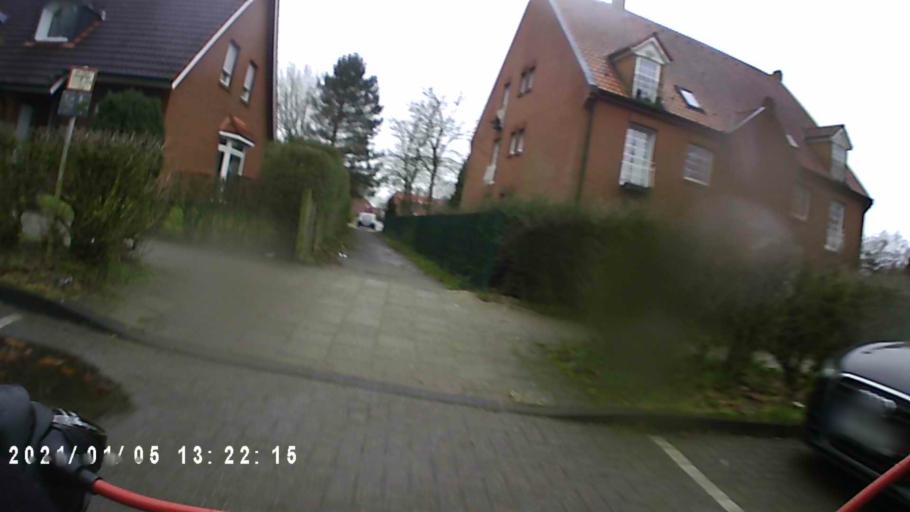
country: DE
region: Lower Saxony
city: Leer
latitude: 53.2325
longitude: 7.4400
